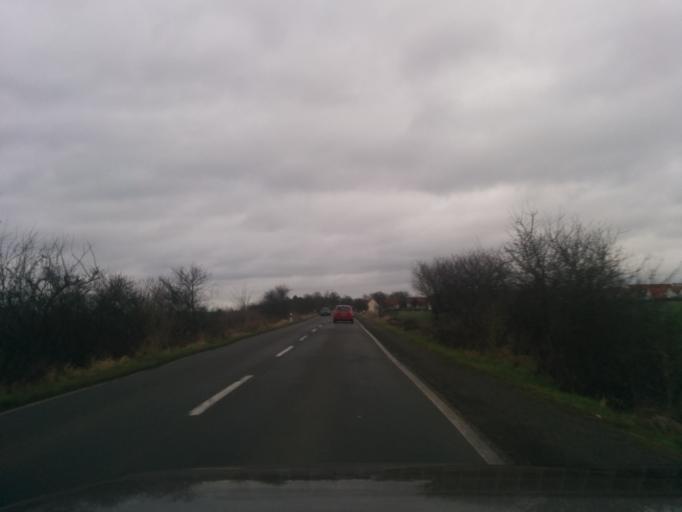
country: DE
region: Saxony-Anhalt
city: Lieskau
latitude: 51.5061
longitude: 11.8700
